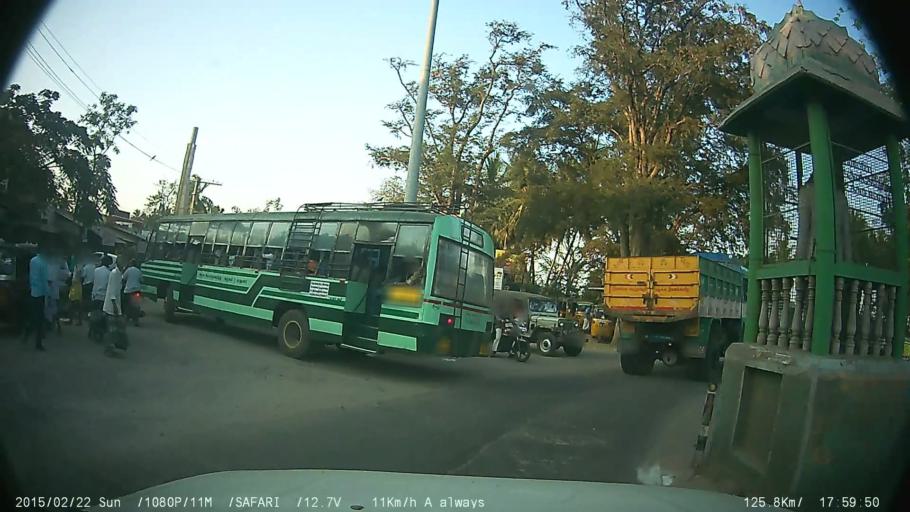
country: IN
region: Tamil Nadu
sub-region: Theni
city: Uttamapalaiyam
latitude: 9.8028
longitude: 77.3285
